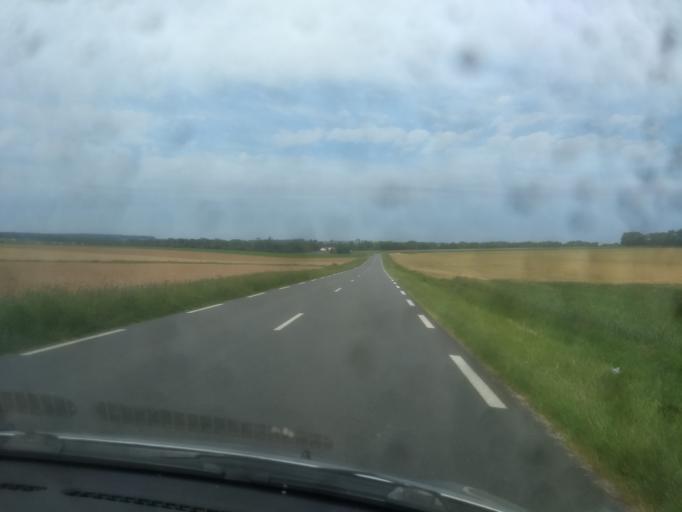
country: FR
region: Picardie
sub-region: Departement de la Somme
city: Saint-Riquier
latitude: 50.1411
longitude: 1.9898
